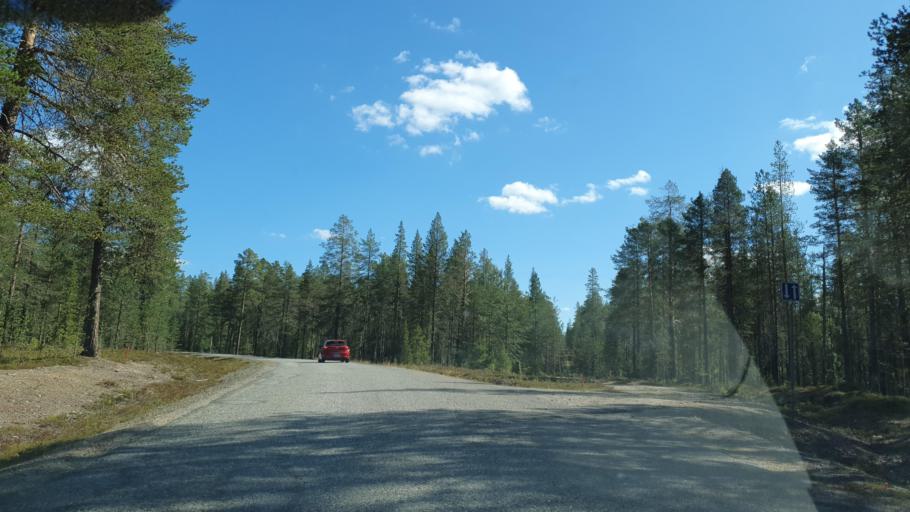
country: FI
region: Lapland
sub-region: Tunturi-Lappi
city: Muonio
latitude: 67.7061
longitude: 24.1433
